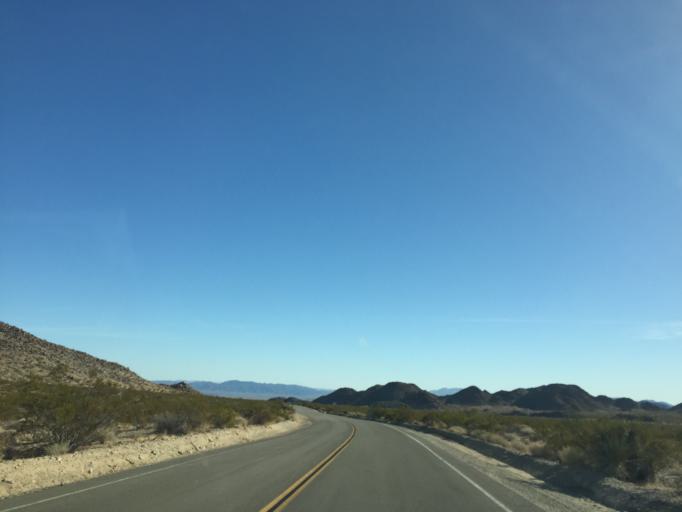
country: US
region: California
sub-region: Riverside County
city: Mecca
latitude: 33.8168
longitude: -115.7661
